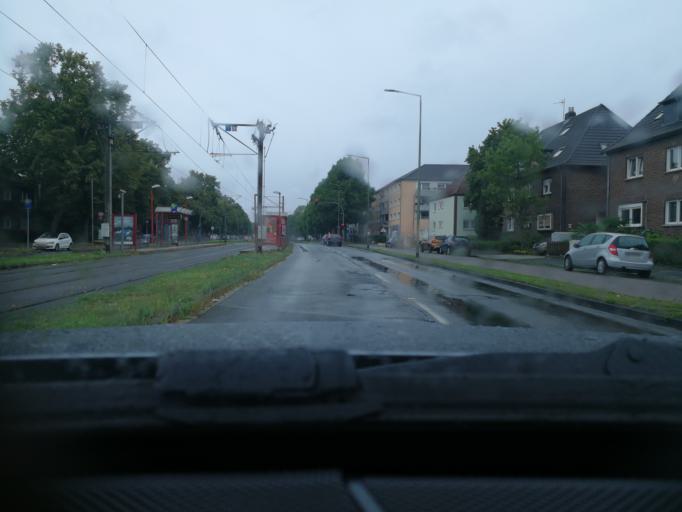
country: DE
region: North Rhine-Westphalia
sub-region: Regierungsbezirk Dusseldorf
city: Dinslaken
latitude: 51.5298
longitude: 6.7430
